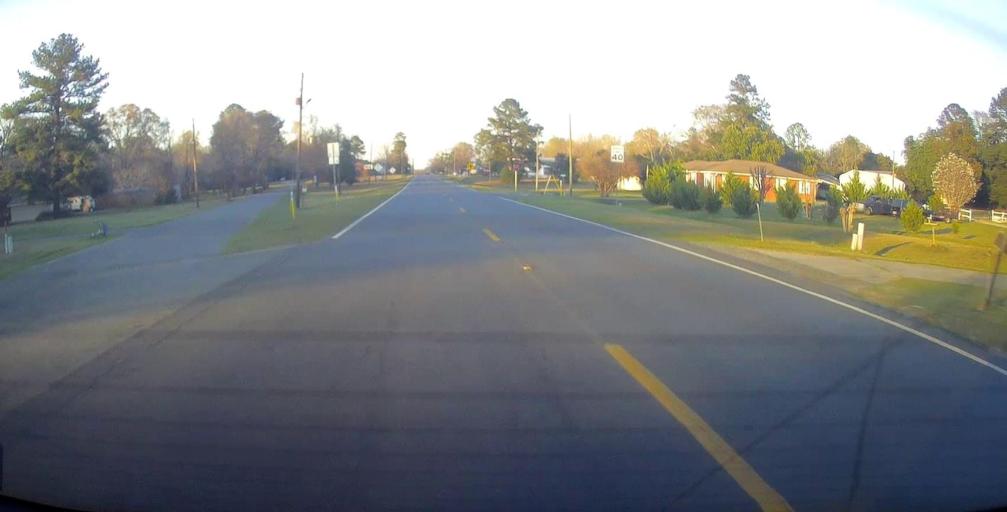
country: US
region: Georgia
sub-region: Dodge County
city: Chester
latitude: 32.3781
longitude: -82.9937
